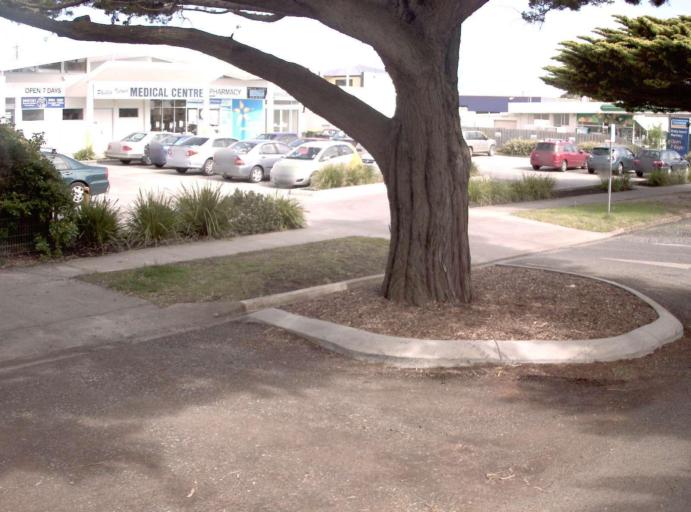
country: AU
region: Victoria
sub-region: Bass Coast
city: Cowes
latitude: -38.4572
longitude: 145.2390
